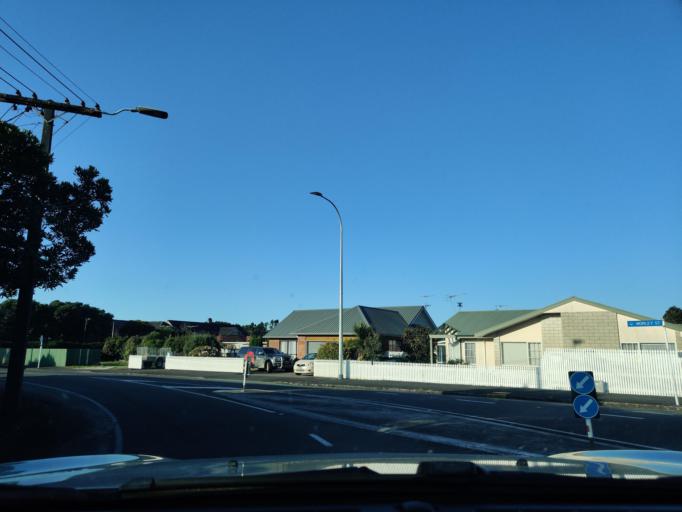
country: NZ
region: Taranaki
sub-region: New Plymouth District
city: New Plymouth
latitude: -39.0669
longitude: 174.0658
